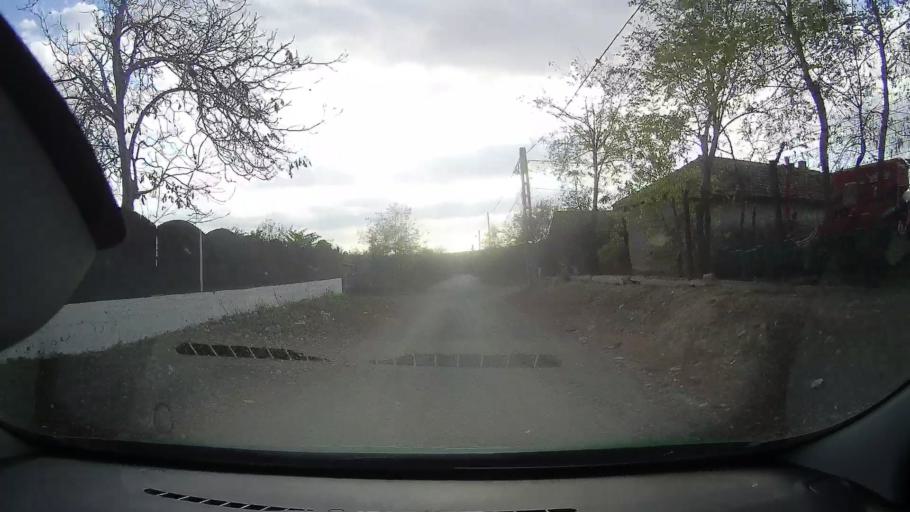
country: RO
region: Constanta
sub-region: Comuna Sacele
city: Sacele
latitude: 44.4899
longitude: 28.6371
